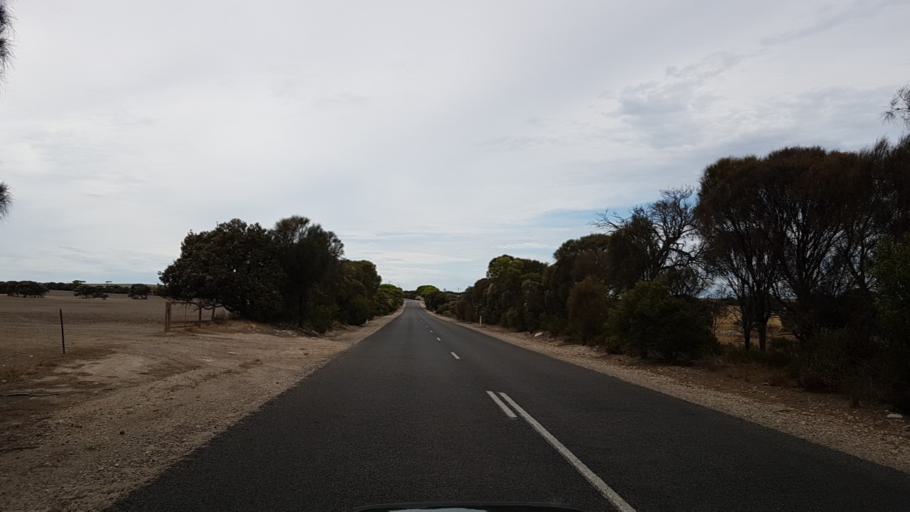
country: AU
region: South Australia
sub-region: Yorke Peninsula
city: Honiton
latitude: -34.9663
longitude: 137.1087
